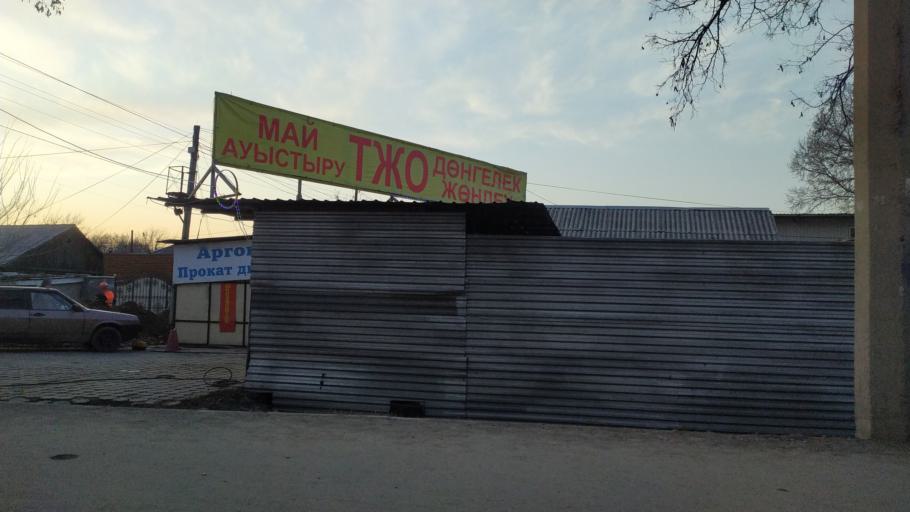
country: KZ
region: Almaty Qalasy
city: Almaty
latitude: 43.2197
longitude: 76.8796
